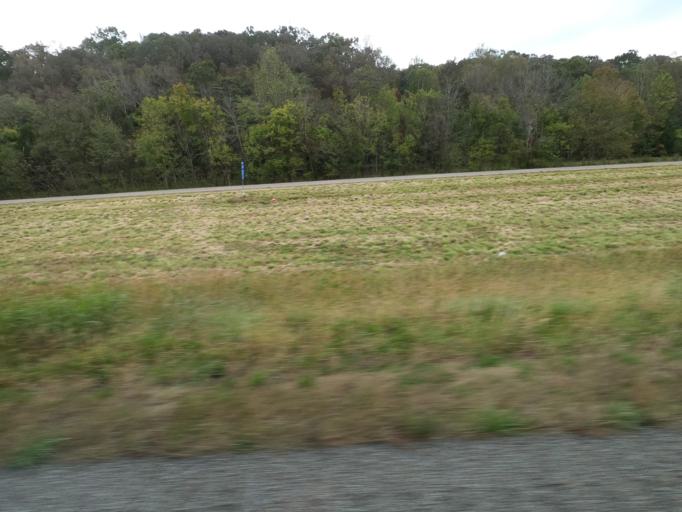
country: US
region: Tennessee
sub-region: Humphreys County
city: Waverly
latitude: 35.8746
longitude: -87.7200
